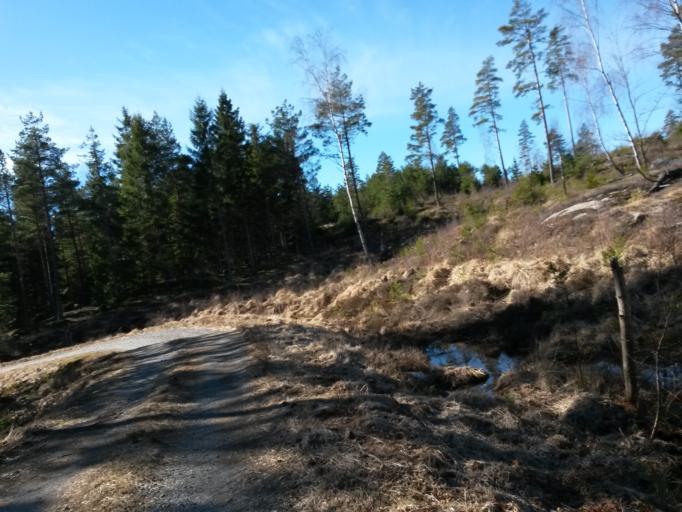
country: SE
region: Vaestra Goetaland
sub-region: Vargarda Kommun
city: Jonstorp
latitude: 57.9637
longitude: 12.6806
